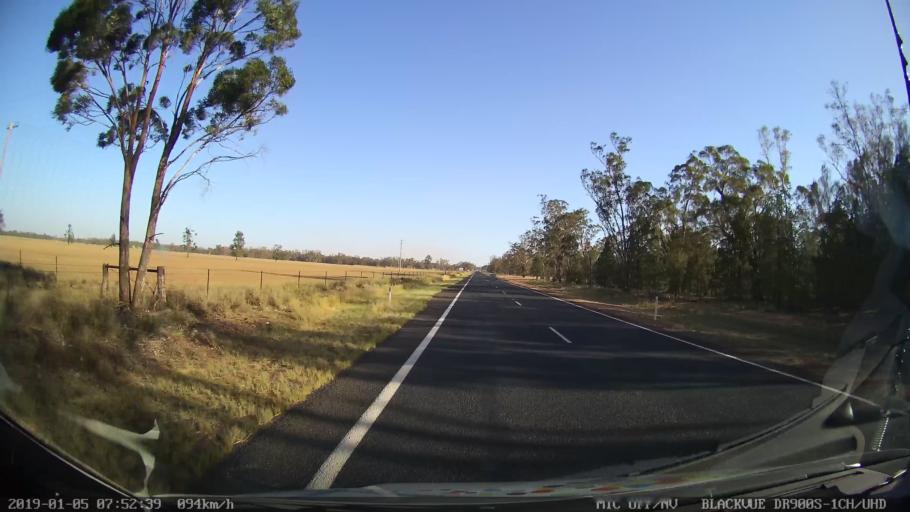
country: AU
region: New South Wales
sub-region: Gilgandra
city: Gilgandra
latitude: -31.7555
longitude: 148.6404
